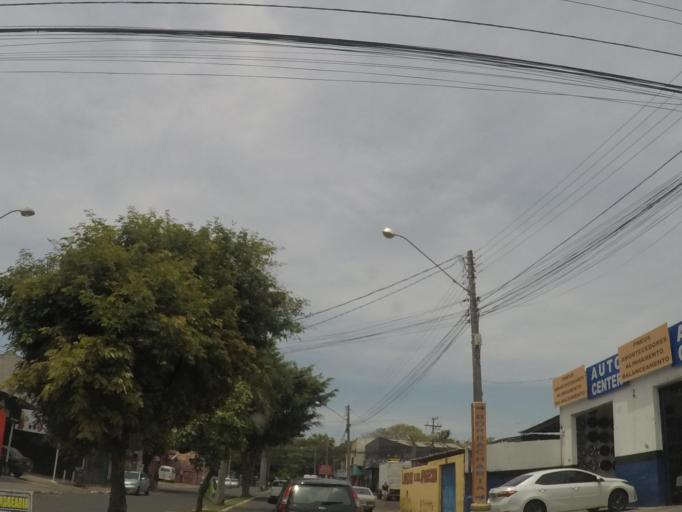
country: BR
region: Sao Paulo
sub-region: Hortolandia
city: Hortolandia
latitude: -22.8512
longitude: -47.1879
